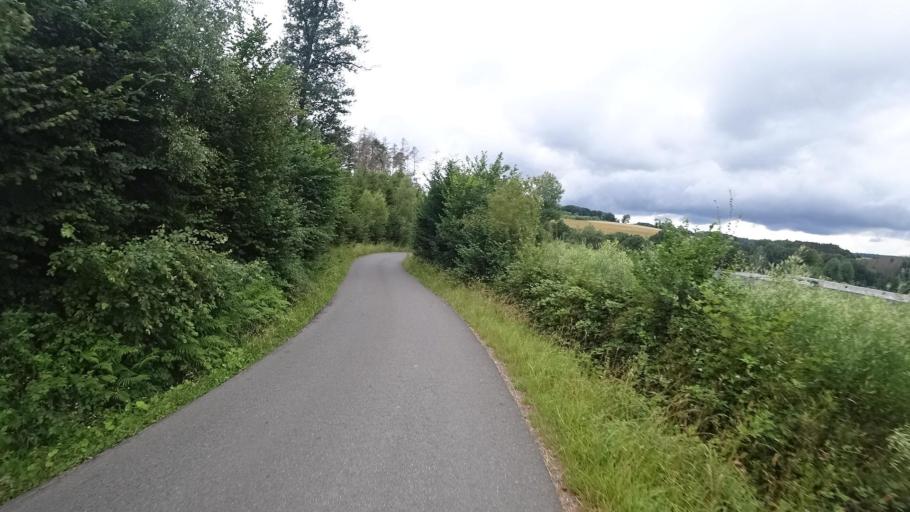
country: DE
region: Rheinland-Pfalz
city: Seifen
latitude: 50.6821
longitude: 7.5085
